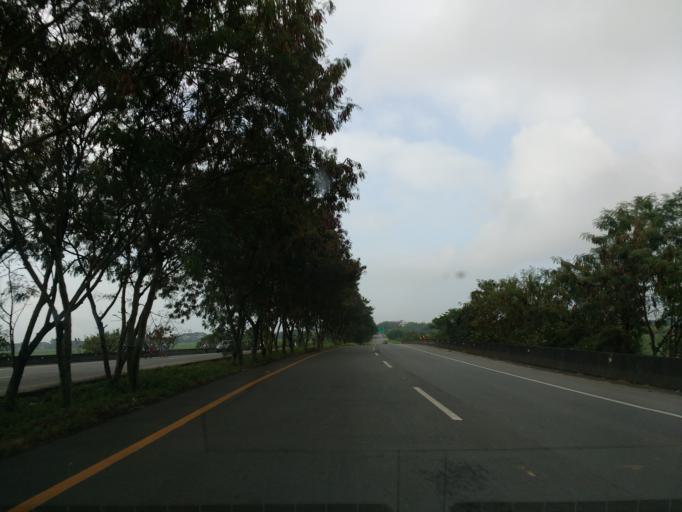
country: CO
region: Valle del Cauca
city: Palmira
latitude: 3.5316
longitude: -76.3376
